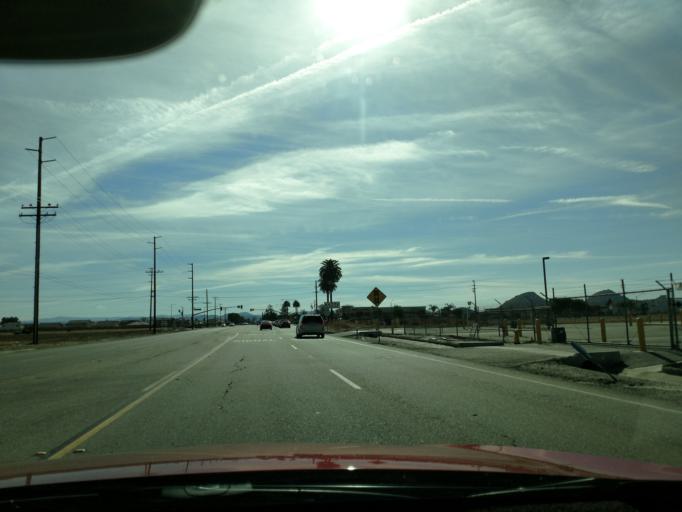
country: US
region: California
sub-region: Riverside County
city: San Jacinto
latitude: 33.7890
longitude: -117.0069
